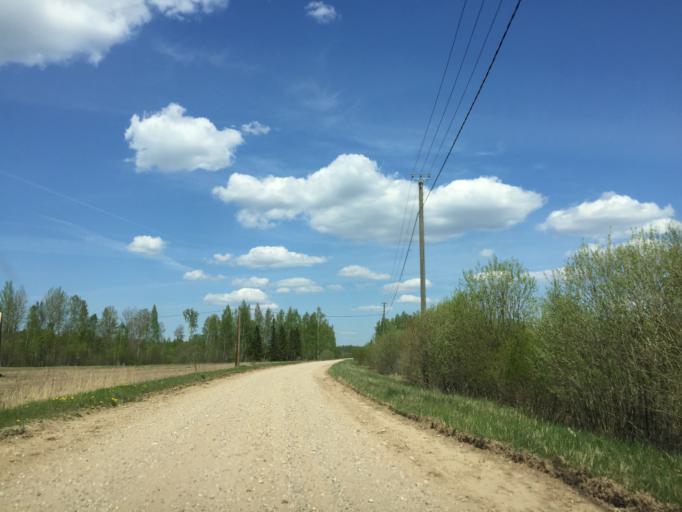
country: LV
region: Limbazu Rajons
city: Limbazi
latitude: 57.3902
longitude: 24.5726
